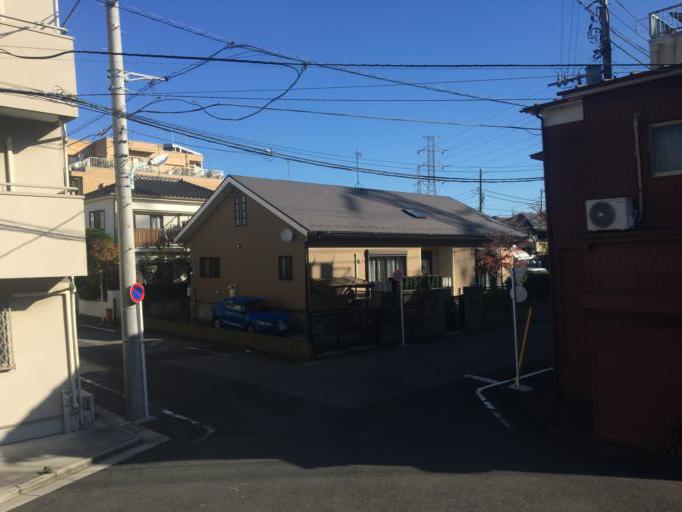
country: JP
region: Chiba
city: Matsudo
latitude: 35.7482
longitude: 139.8750
